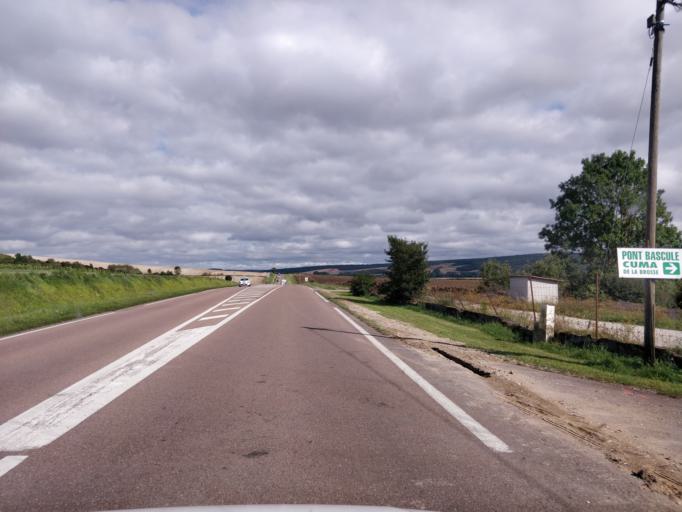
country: FR
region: Champagne-Ardenne
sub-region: Departement de l'Aube
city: Aix-en-Othe
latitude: 48.2334
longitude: 3.6285
